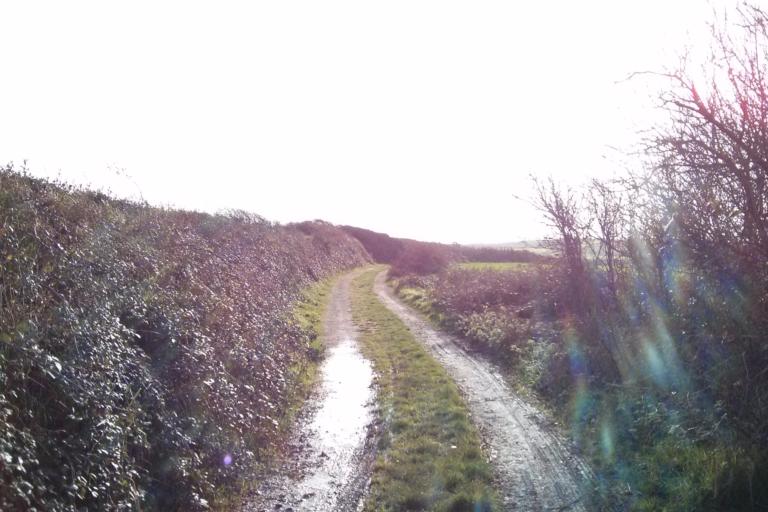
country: FR
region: Brittany
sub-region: Departement du Finistere
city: Le Conquet
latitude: 48.3998
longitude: -4.7710
